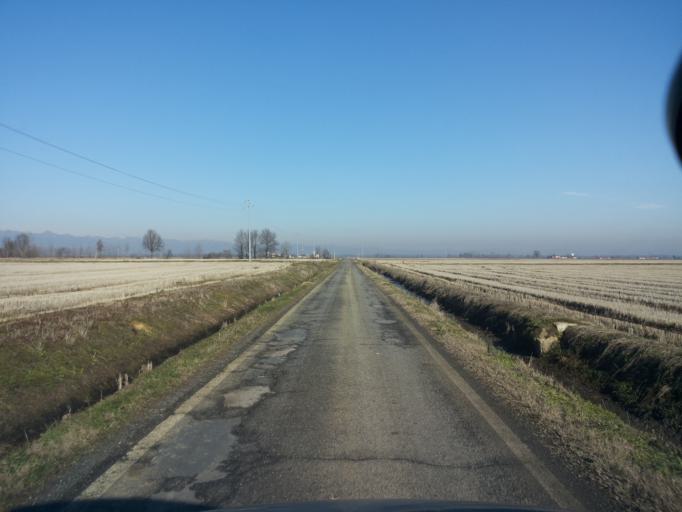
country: IT
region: Piedmont
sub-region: Provincia di Vercelli
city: Formigliana
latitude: 45.4228
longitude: 8.2536
